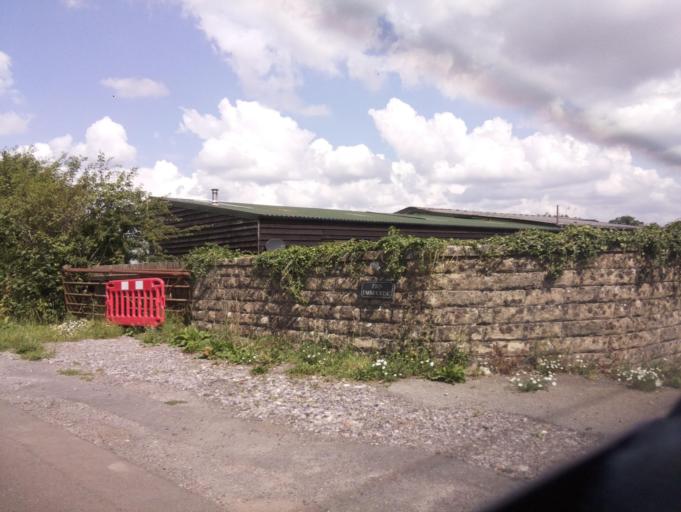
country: GB
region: England
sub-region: Wiltshire
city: Charlton
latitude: 51.5675
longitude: -2.0650
